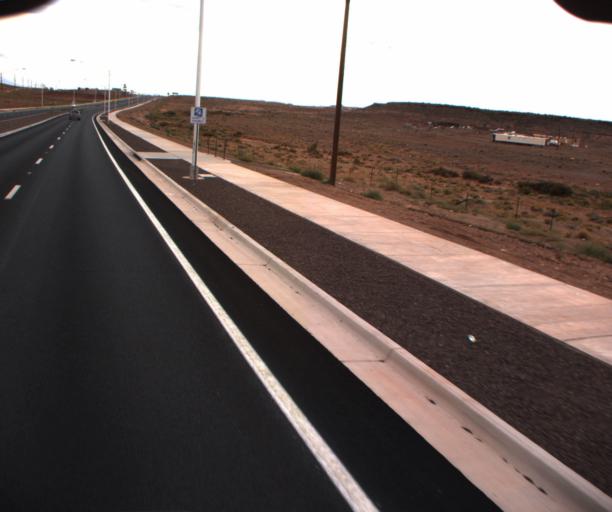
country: US
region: Arizona
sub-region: Coconino County
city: Tuba City
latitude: 35.8640
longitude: -111.4169
